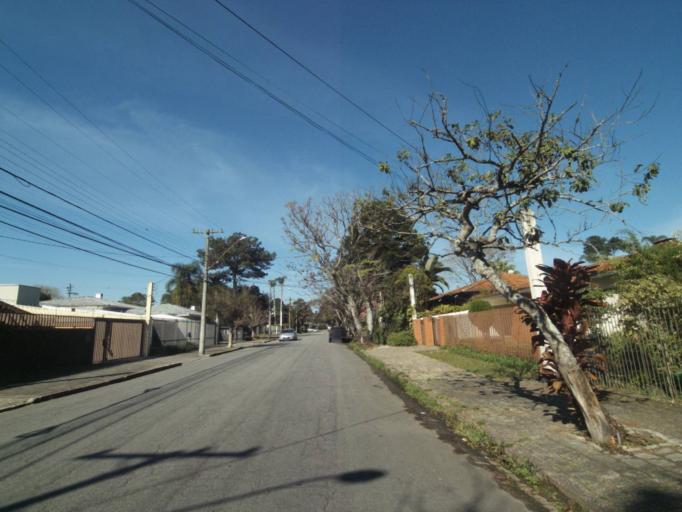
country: BR
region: Parana
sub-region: Curitiba
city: Curitiba
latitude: -25.4171
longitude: -49.2299
